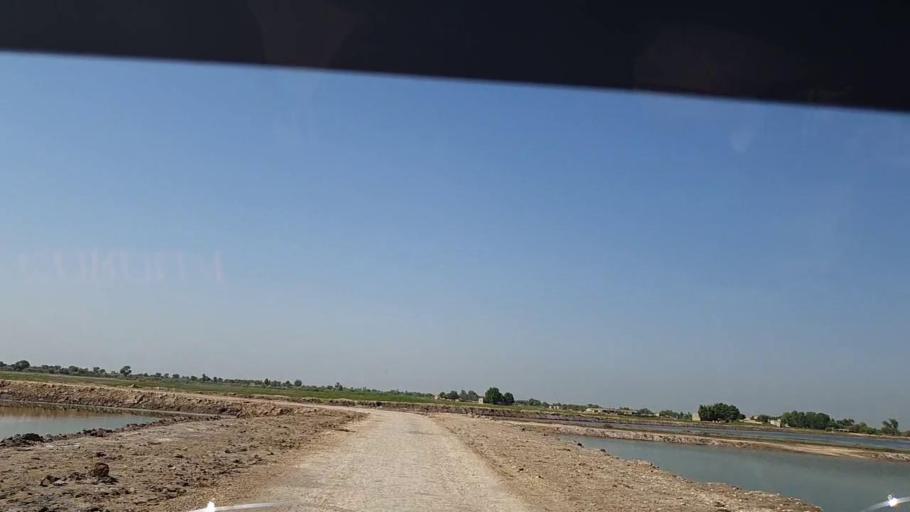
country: PK
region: Sindh
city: Tangwani
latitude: 28.3247
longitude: 69.0838
